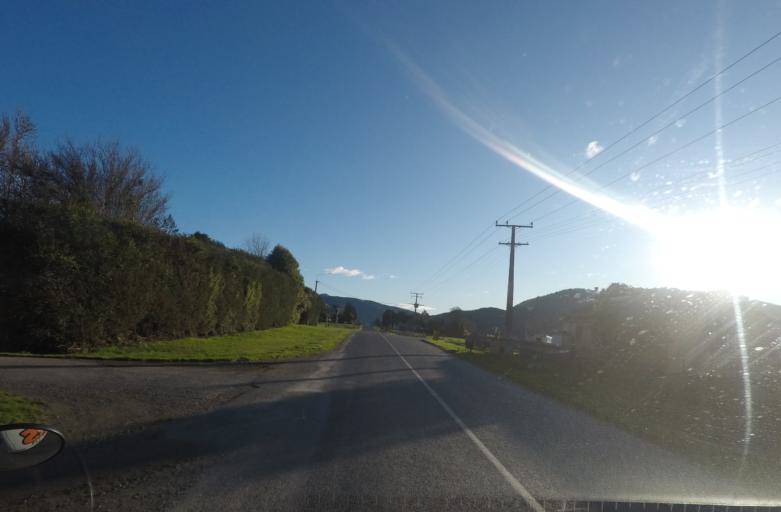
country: NZ
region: Marlborough
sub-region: Marlborough District
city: Picton
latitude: -41.2894
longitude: 173.8687
